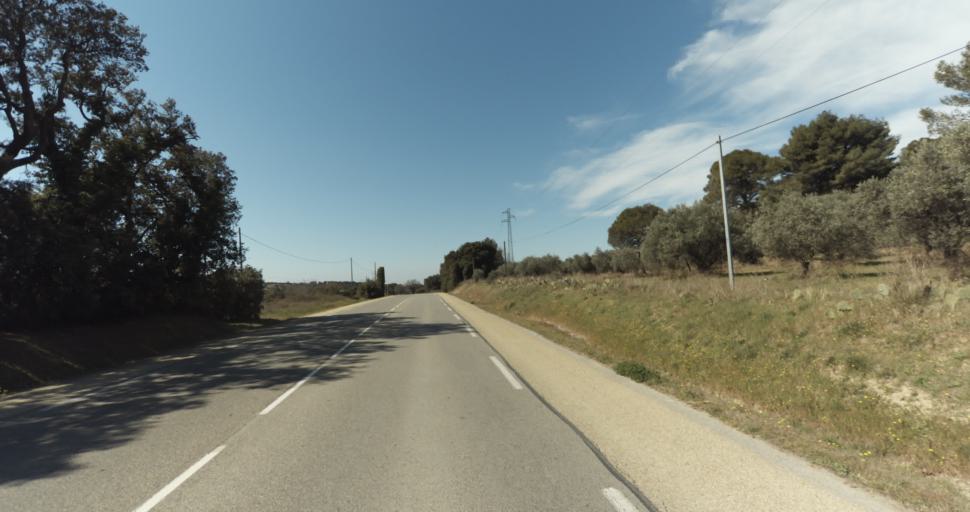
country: FR
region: Provence-Alpes-Cote d'Azur
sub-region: Departement des Bouches-du-Rhone
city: Vernegues
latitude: 43.6473
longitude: 5.2088
